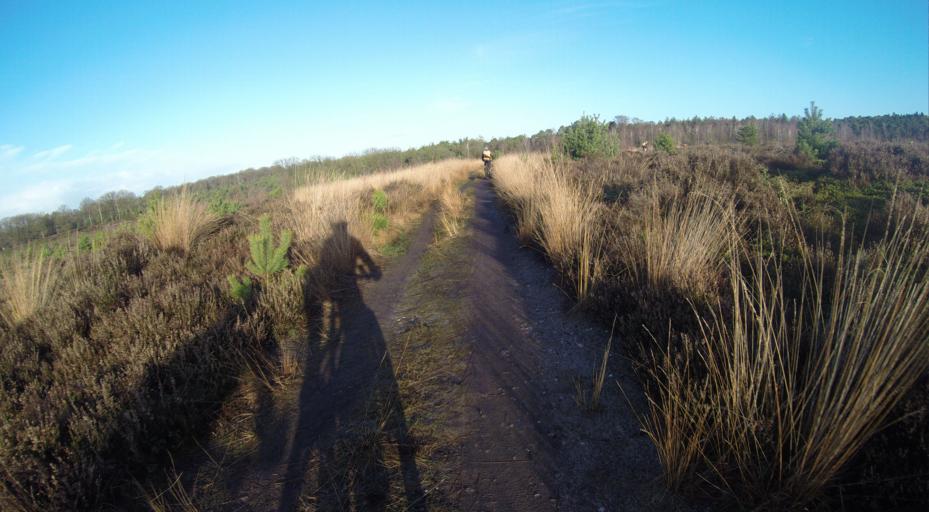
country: NL
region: Overijssel
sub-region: Gemeente Hof van Twente
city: Markelo
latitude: 52.3229
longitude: 6.4111
